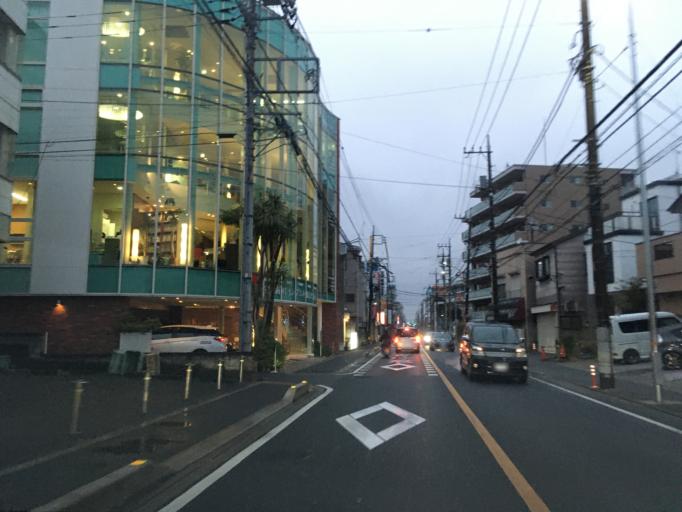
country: JP
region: Saitama
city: Asaka
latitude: 35.7863
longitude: 139.6001
